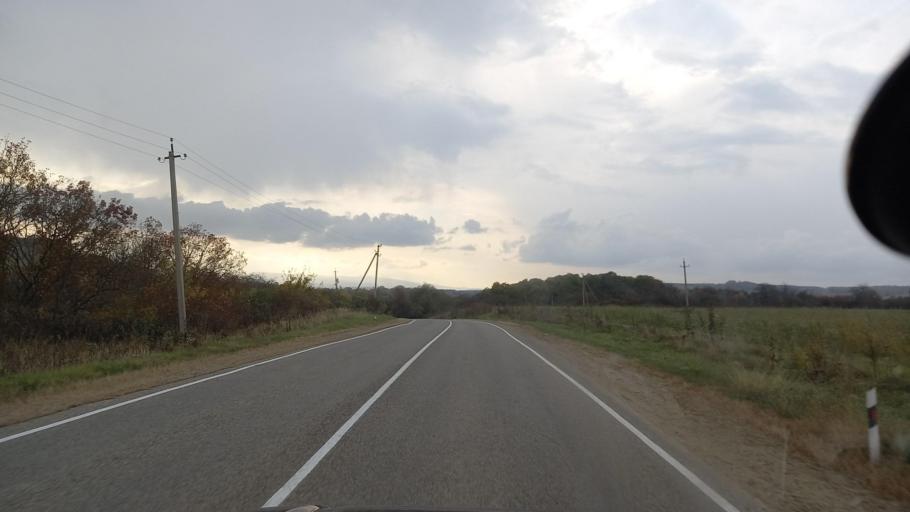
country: RU
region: Krasnodarskiy
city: Perepravnaya
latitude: 44.3755
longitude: 40.7358
